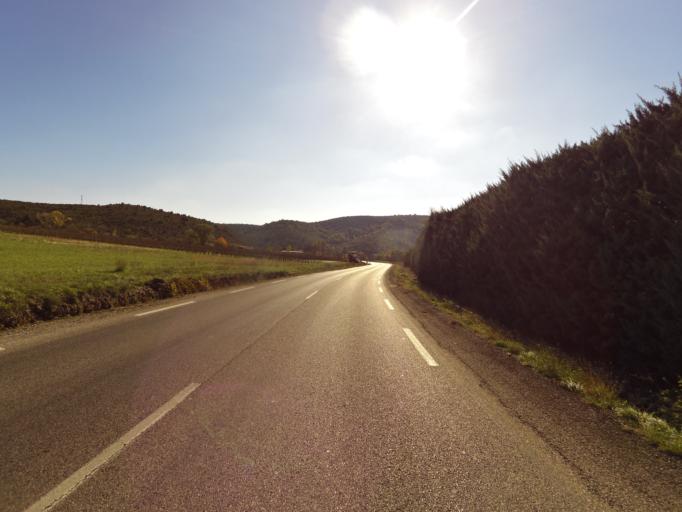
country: FR
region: Rhone-Alpes
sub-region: Departement de l'Ardeche
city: Largentiere
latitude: 44.5283
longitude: 4.3391
